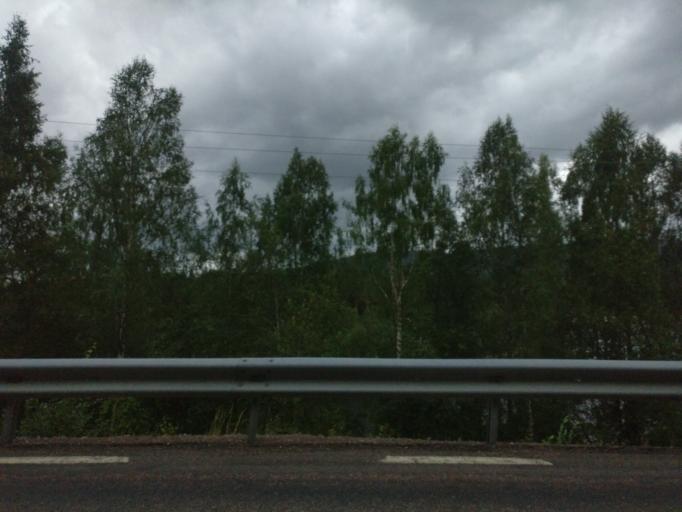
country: SE
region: Vaermland
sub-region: Torsby Kommun
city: Torsby
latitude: 60.5926
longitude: 13.0740
